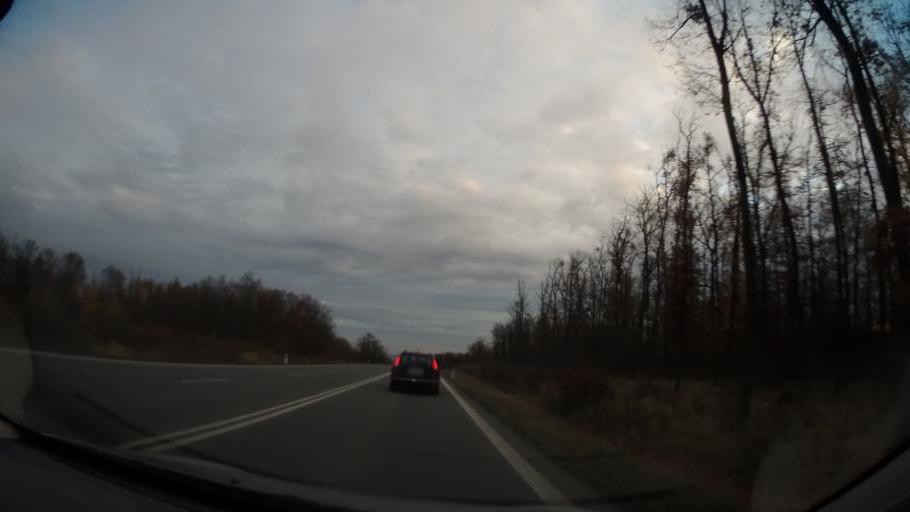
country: CZ
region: South Moravian
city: Troubsko
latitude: 49.1891
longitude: 16.4626
